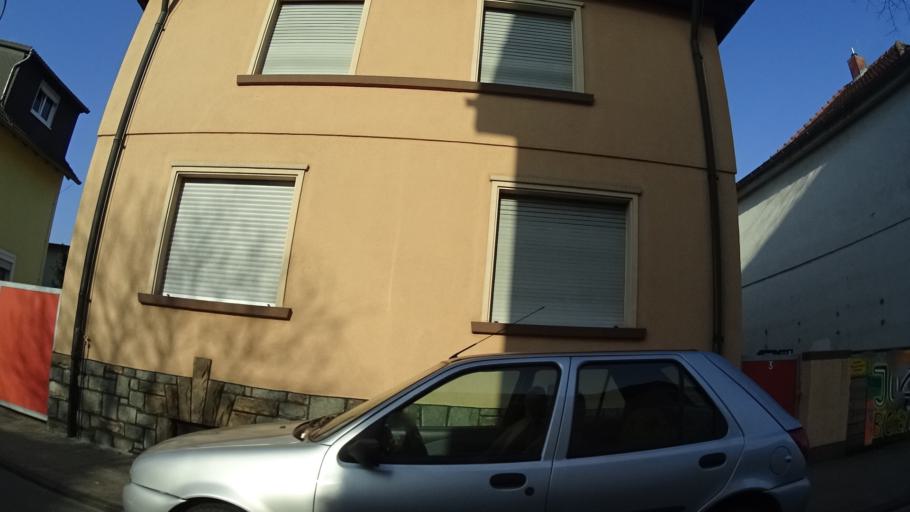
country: DE
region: Hesse
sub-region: Regierungsbezirk Darmstadt
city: Bickenbach
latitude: 49.7559
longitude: 8.6115
